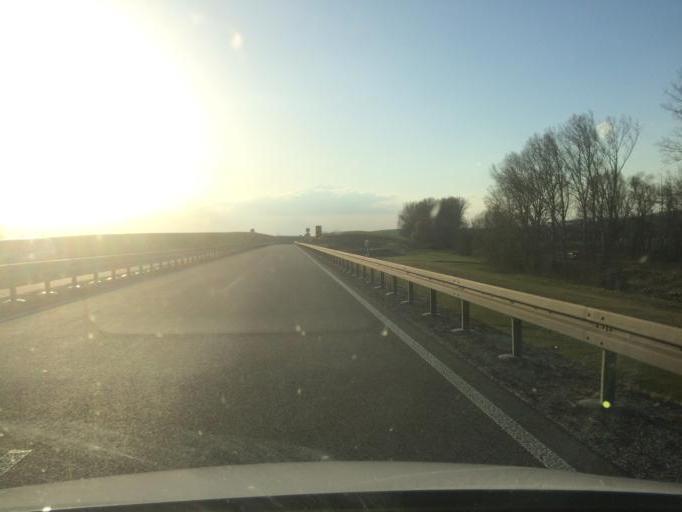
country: DE
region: Thuringia
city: Wipperdorf
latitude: 51.5028
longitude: 10.6996
